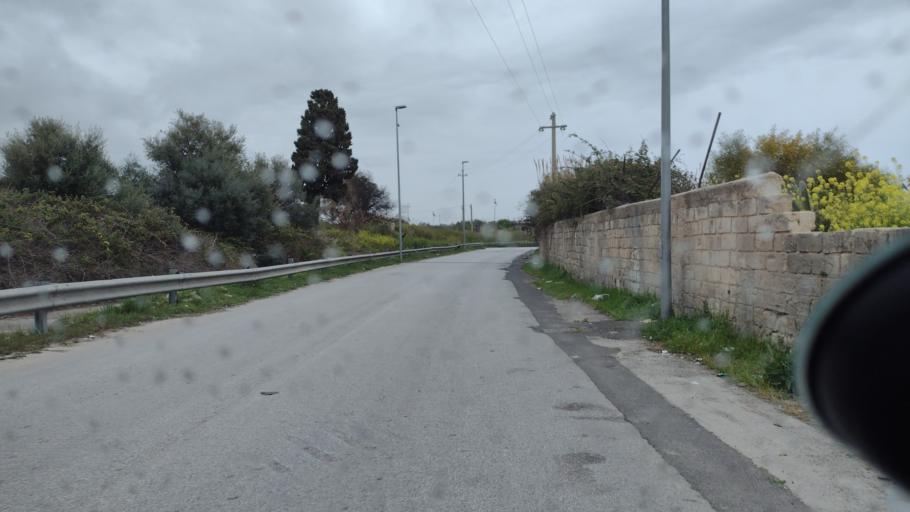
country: IT
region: Sicily
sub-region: Provincia di Siracusa
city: Avola
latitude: 36.9201
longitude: 15.1405
